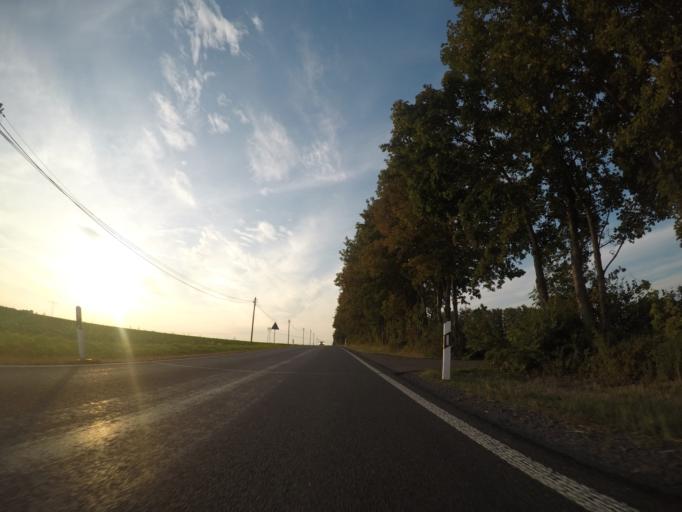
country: DE
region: Thuringia
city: Altkirchen
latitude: 50.9241
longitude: 12.3340
